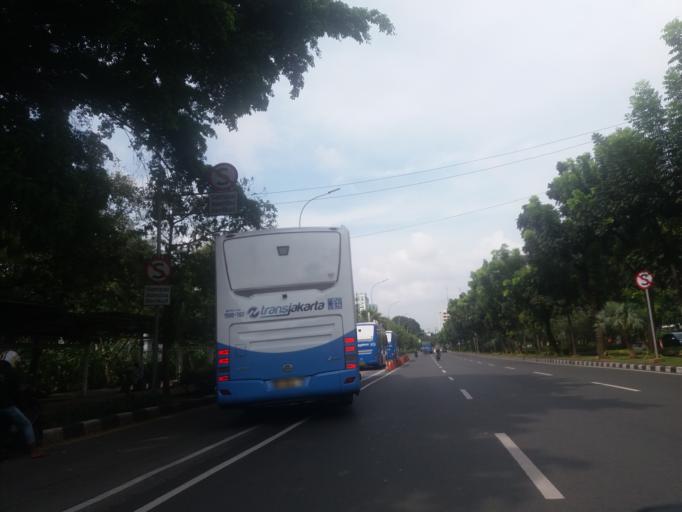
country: ID
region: Jakarta Raya
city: Jakarta
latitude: -6.1804
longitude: 106.8271
